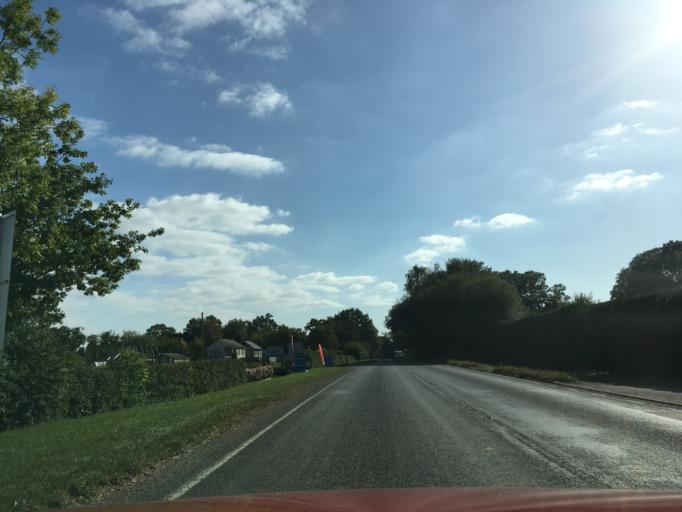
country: GB
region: England
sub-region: Hampshire
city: Tadley
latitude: 51.3314
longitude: -1.1281
